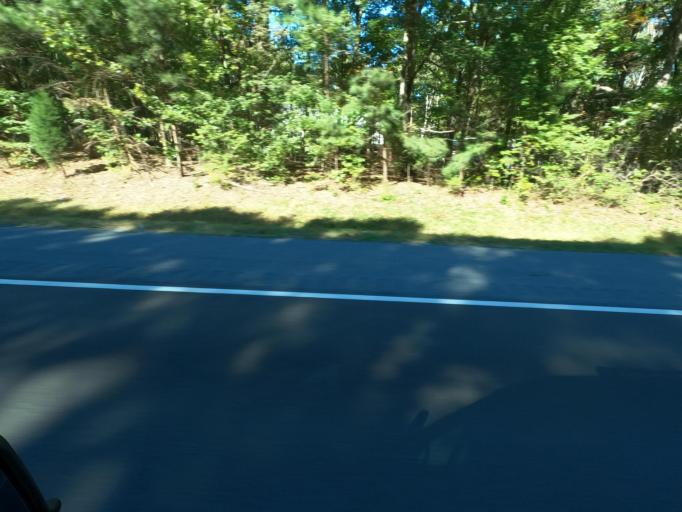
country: US
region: Tennessee
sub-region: Cheatham County
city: Kingston Springs
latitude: 36.0502
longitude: -87.1427
